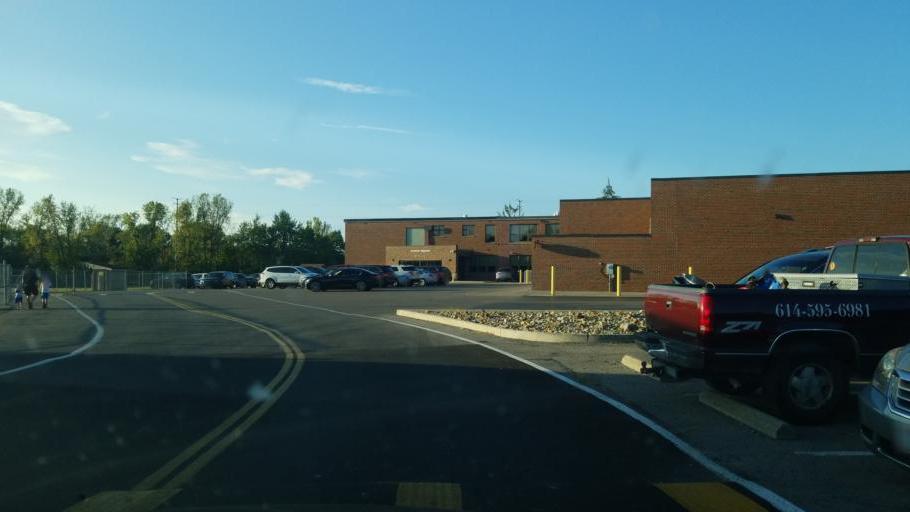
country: US
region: Ohio
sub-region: Delaware County
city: Lewis Center
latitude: 40.2113
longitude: -83.0228
